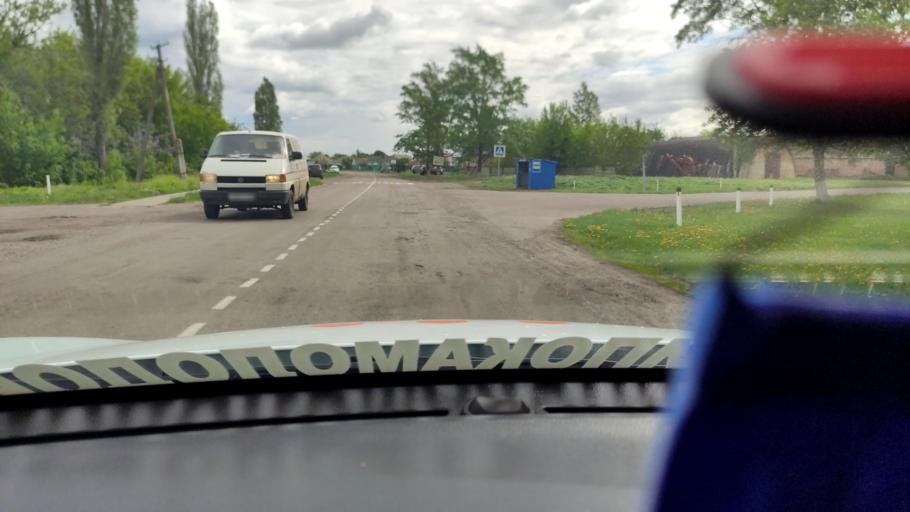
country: RU
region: Voronezj
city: Imeni Pervogo Maya
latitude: 50.6872
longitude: 39.5060
